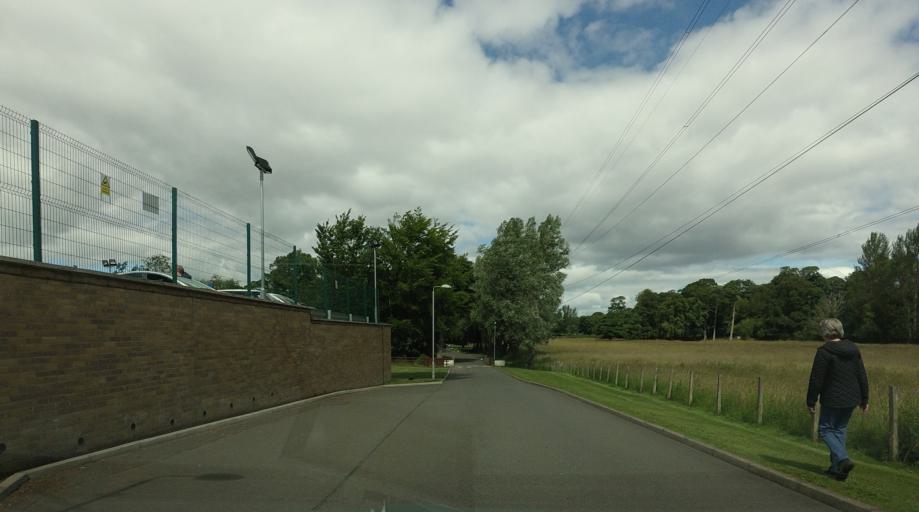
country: GB
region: Scotland
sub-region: Midlothian
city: Loanhead
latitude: 55.9008
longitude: -3.1765
